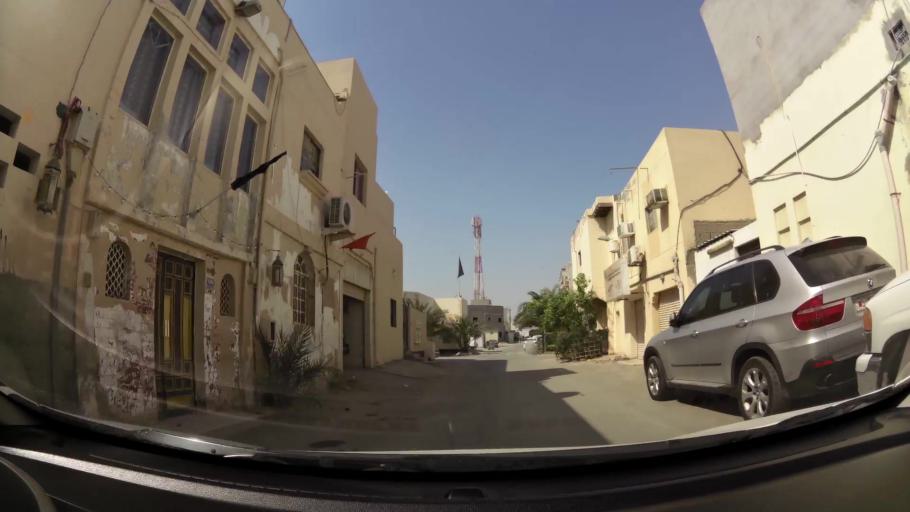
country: BH
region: Northern
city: Madinat `Isa
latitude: 26.1960
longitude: 50.4648
